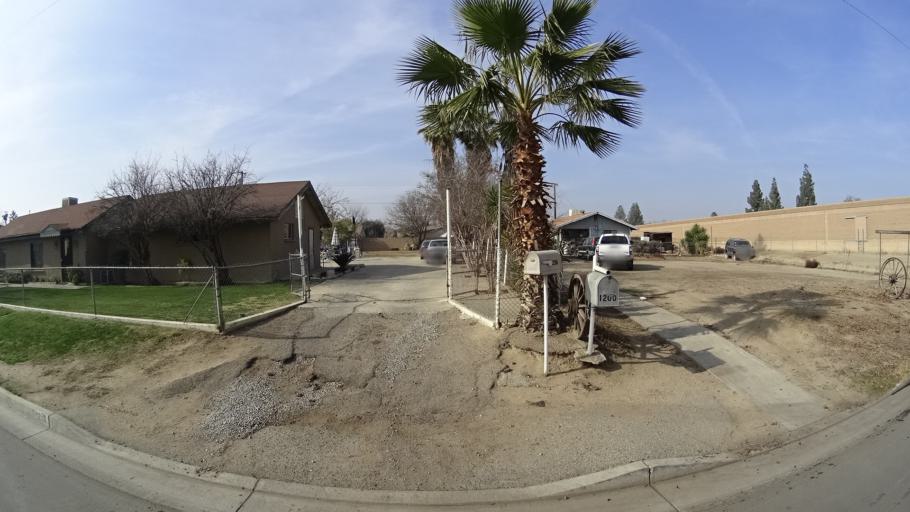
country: US
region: California
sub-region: Kern County
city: Bakersfield
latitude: 35.3519
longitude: -119.0156
